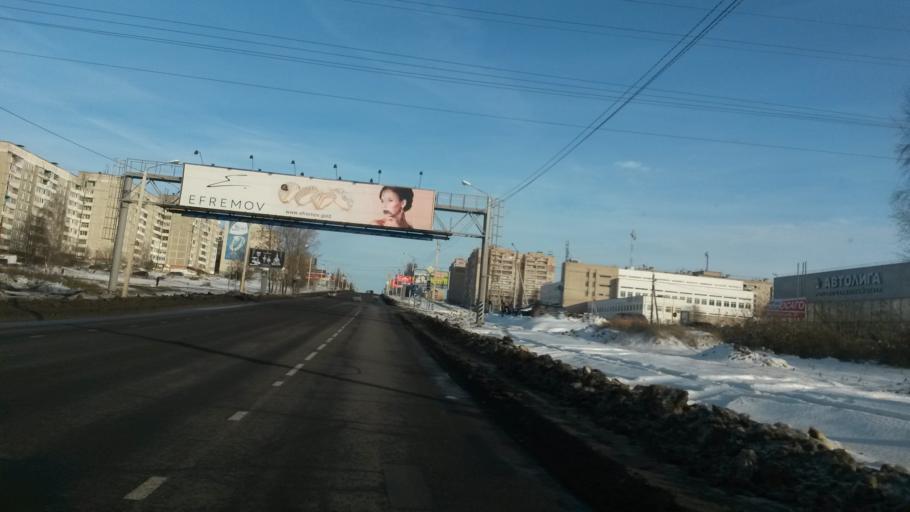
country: RU
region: Kostroma
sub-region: Kostromskoy Rayon
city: Kostroma
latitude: 57.7314
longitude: 40.9036
